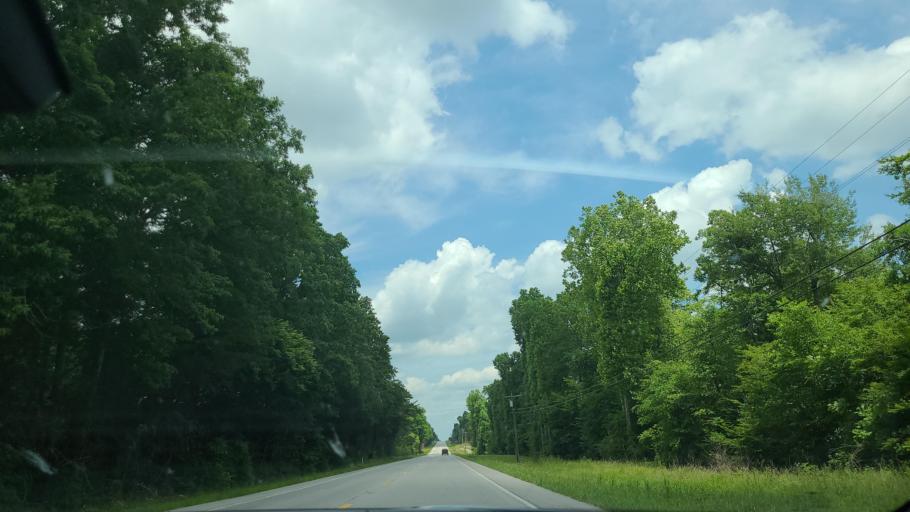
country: US
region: Tennessee
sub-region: Cumberland County
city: Lake Tansi
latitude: 35.7876
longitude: -85.0290
